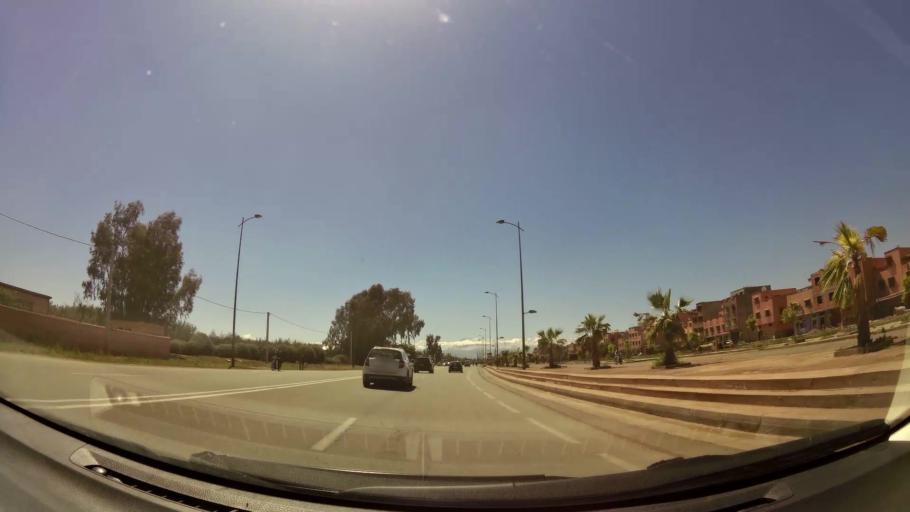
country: MA
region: Marrakech-Tensift-Al Haouz
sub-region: Marrakech
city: Marrakesh
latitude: 31.5657
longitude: -7.9800
